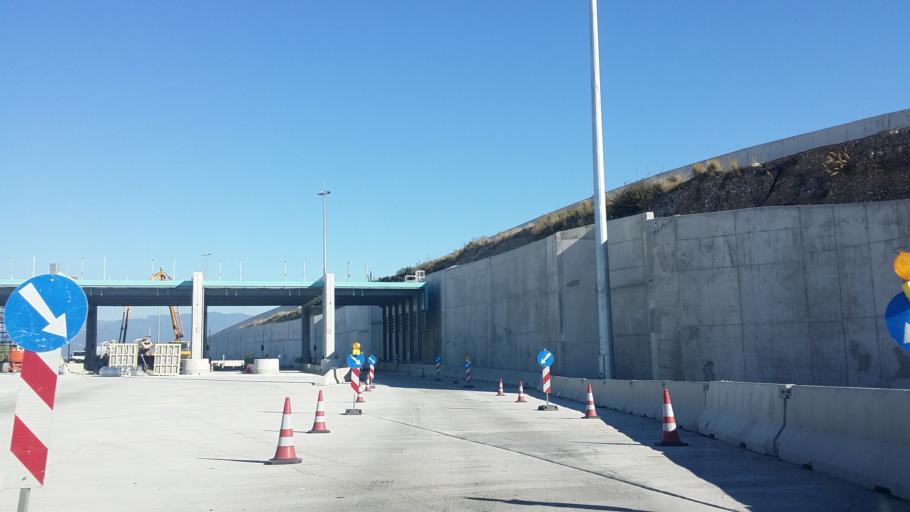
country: GR
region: West Greece
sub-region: Nomos Achaias
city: Rio
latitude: 38.3156
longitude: 21.8298
